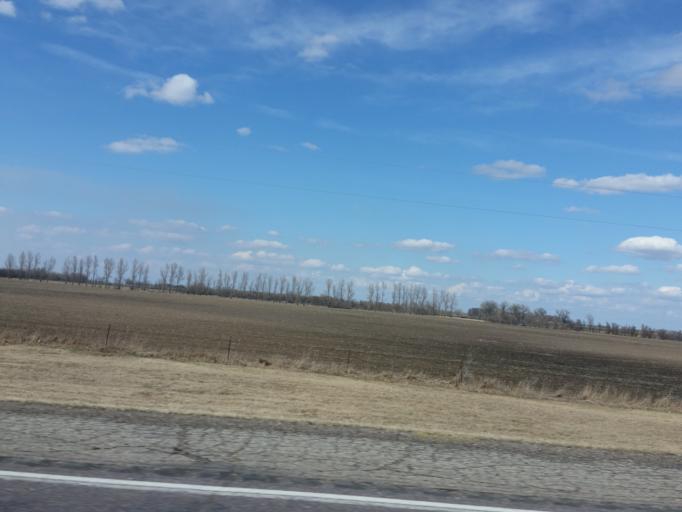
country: US
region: Minnesota
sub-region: Lac qui Parle County
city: Madison
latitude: 44.9360
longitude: -96.2094
